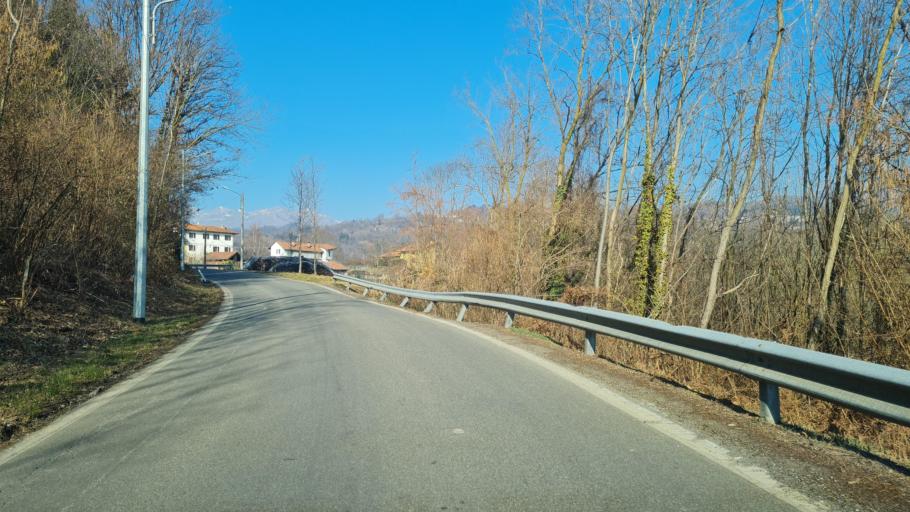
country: IT
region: Piedmont
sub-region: Provincia di Biella
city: Piatto
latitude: 45.5943
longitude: 8.1291
